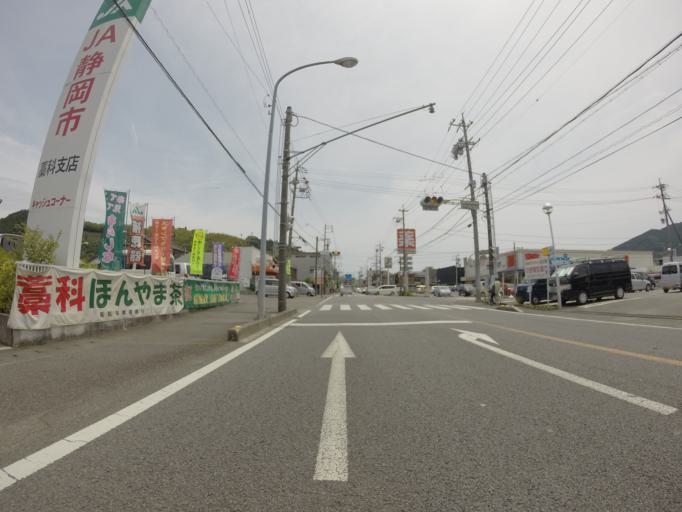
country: JP
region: Shizuoka
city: Shizuoka-shi
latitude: 34.9805
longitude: 138.3424
